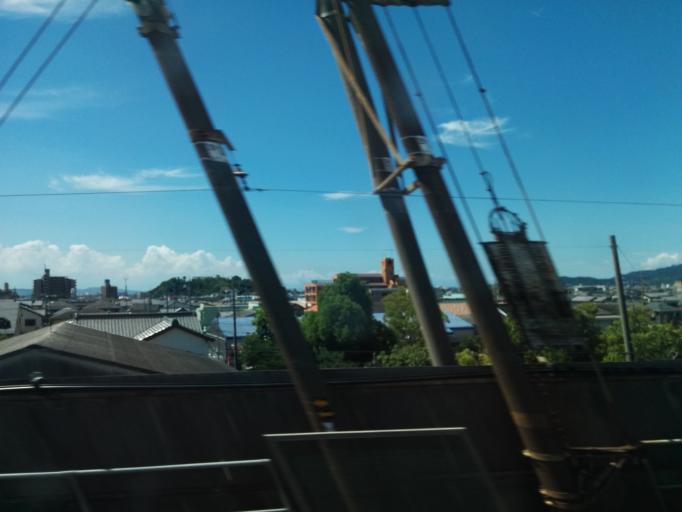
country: JP
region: Aichi
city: Gamagori
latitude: 34.8251
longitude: 137.2428
